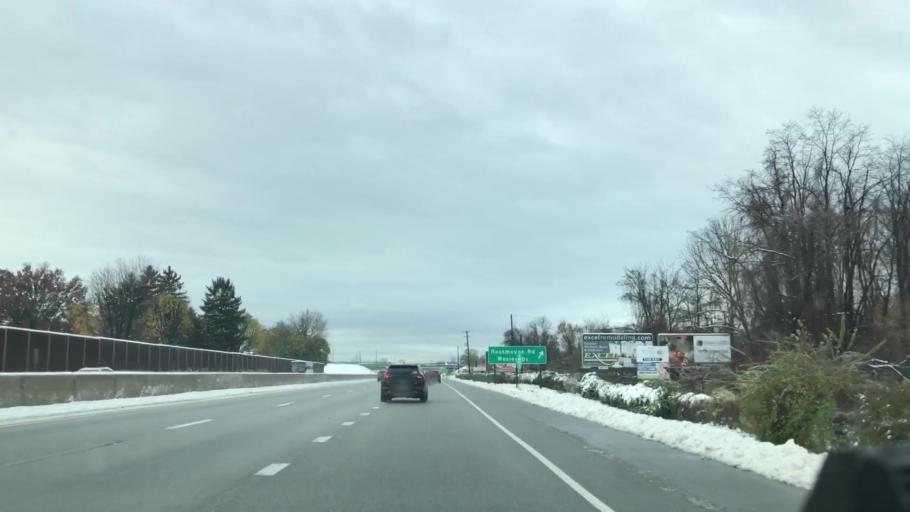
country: US
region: Pennsylvania
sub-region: Cumberland County
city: Shiremanstown
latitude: 40.2121
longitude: -76.9524
